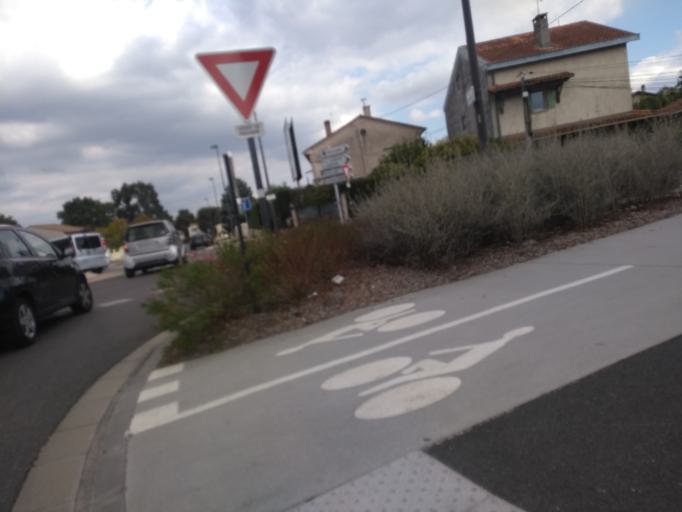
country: FR
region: Aquitaine
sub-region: Departement de la Gironde
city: Talence
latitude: 44.7975
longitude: -0.5810
